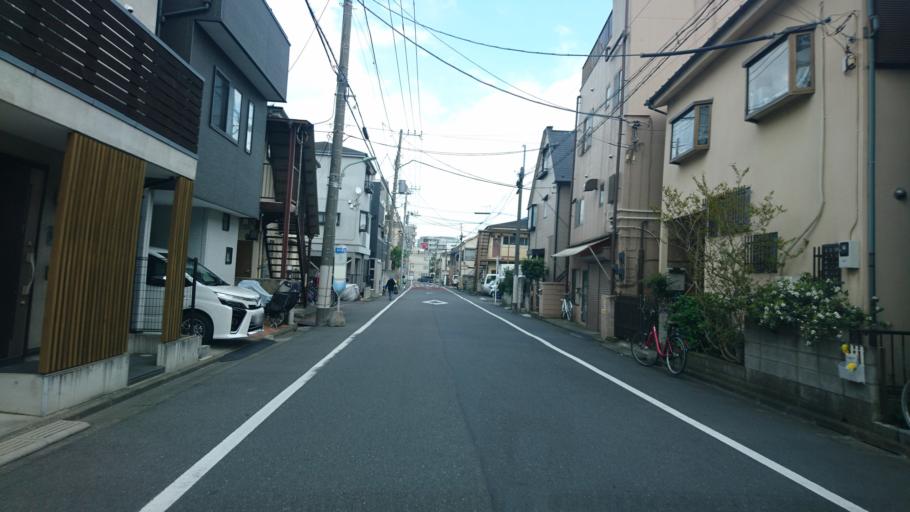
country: JP
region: Kanagawa
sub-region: Kawasaki-shi
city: Kawasaki
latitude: 35.5593
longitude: 139.7056
